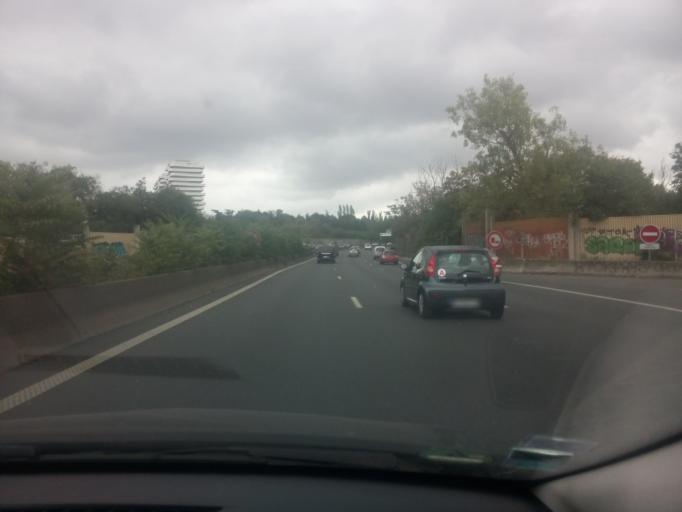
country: FR
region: Ile-de-France
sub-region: Departement du Val-de-Marne
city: Gentilly
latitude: 48.8083
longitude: 2.3401
